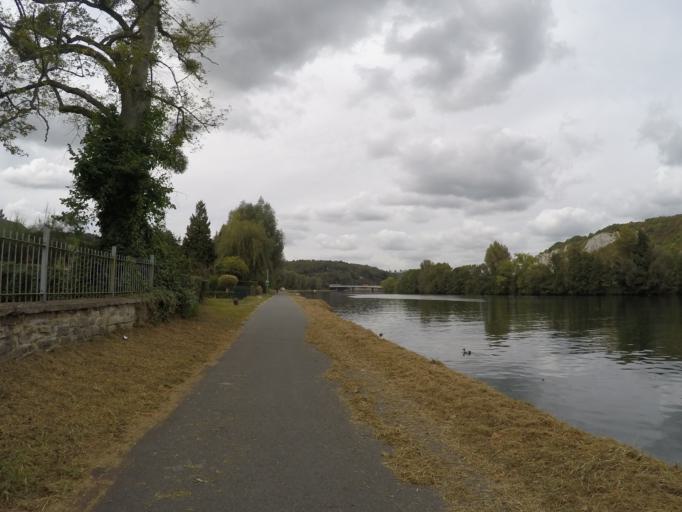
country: BE
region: Wallonia
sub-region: Province de Namur
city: Anhee
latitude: 50.3103
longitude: 4.8830
